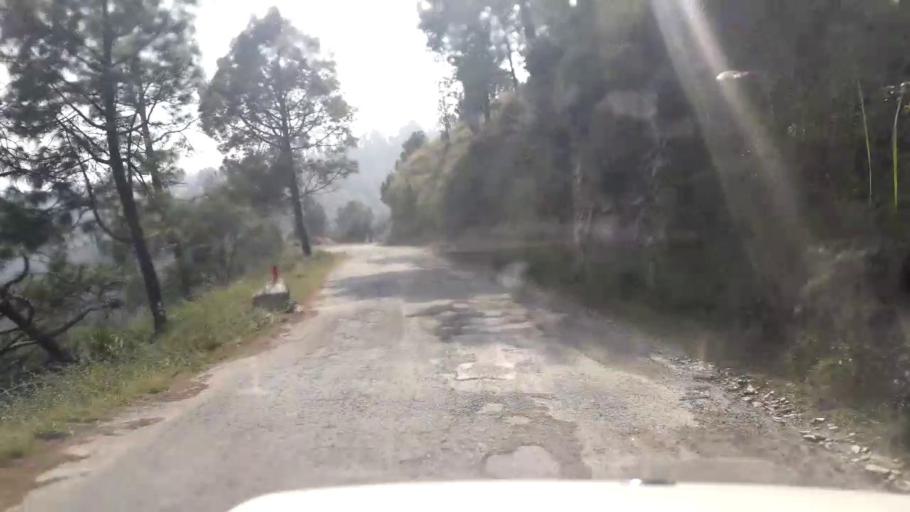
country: IN
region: Himachal Pradesh
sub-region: Shimla
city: Shimla
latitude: 31.0516
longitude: 77.1541
